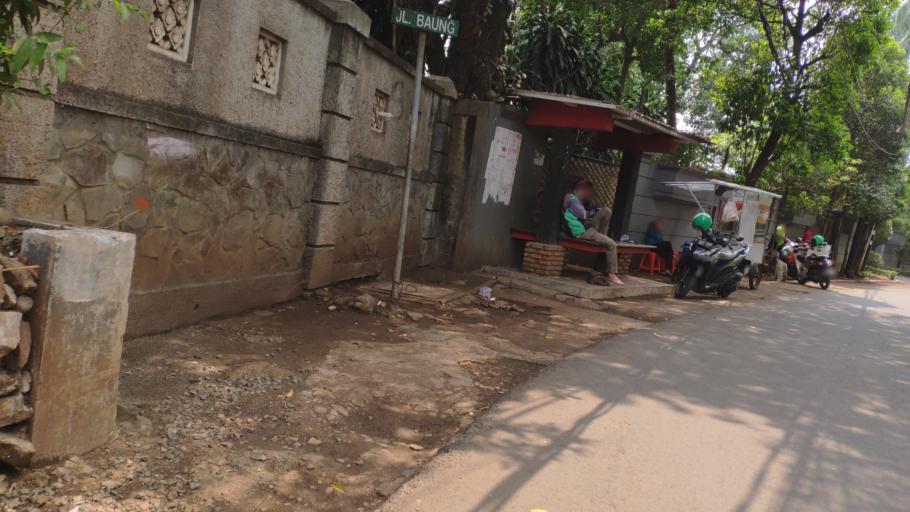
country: ID
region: Jakarta Raya
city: Jakarta
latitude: -6.3044
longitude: 106.8329
